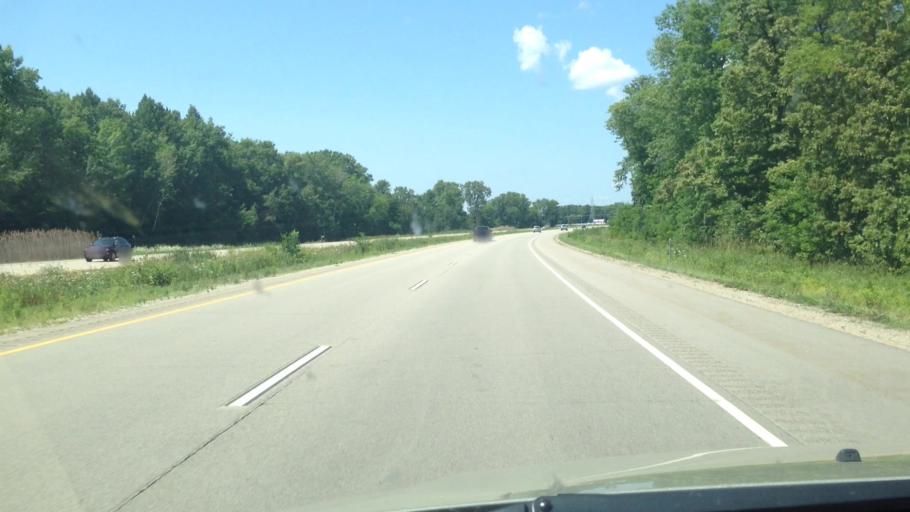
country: US
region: Wisconsin
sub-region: Oconto County
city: Oconto
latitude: 44.8020
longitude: -87.9850
